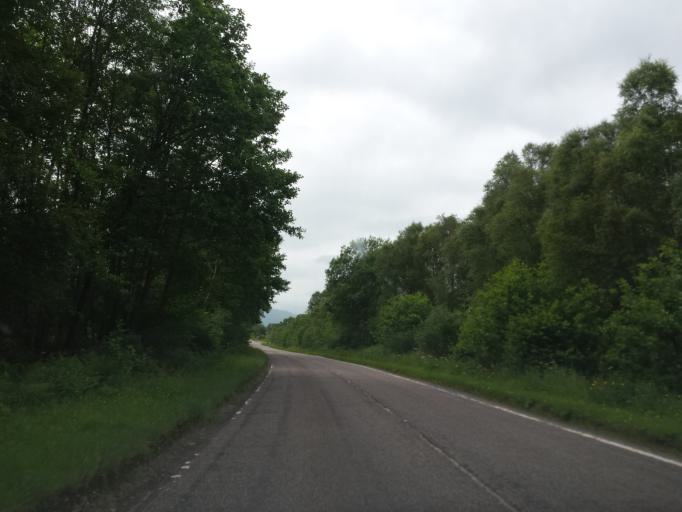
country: GB
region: Scotland
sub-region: Highland
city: Fort William
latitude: 56.8551
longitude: -5.2681
